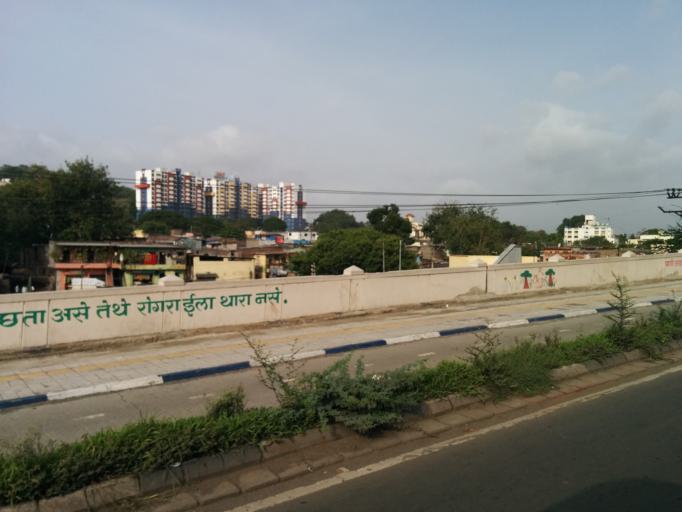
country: IN
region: Maharashtra
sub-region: Pune Division
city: Pune
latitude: 18.5054
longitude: 73.9163
